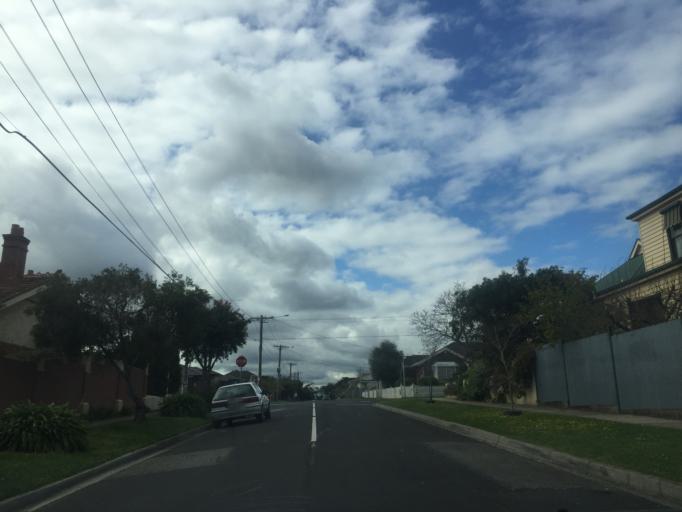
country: AU
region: Victoria
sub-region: Darebin
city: Reservoir
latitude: -37.7268
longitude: 145.0089
